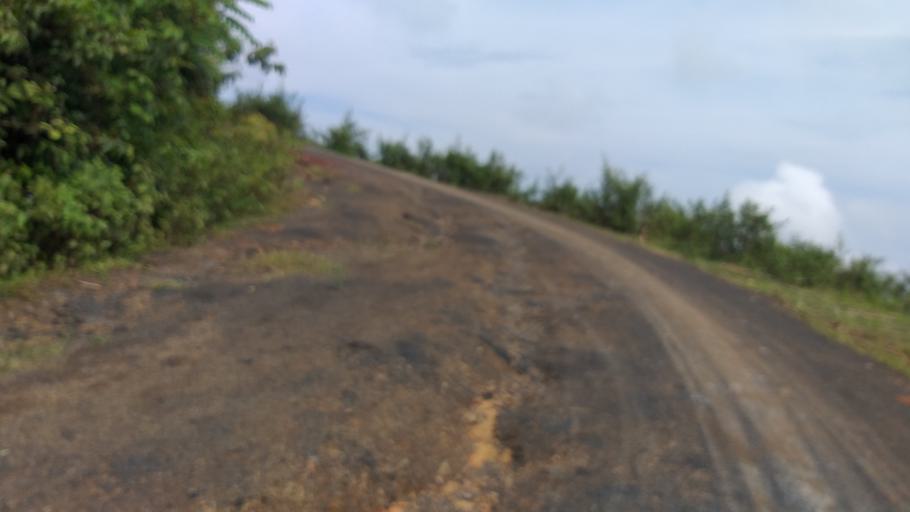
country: VN
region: Huyen Dien Bien
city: Dien Bien Phu
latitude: 21.4078
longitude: 102.6827
